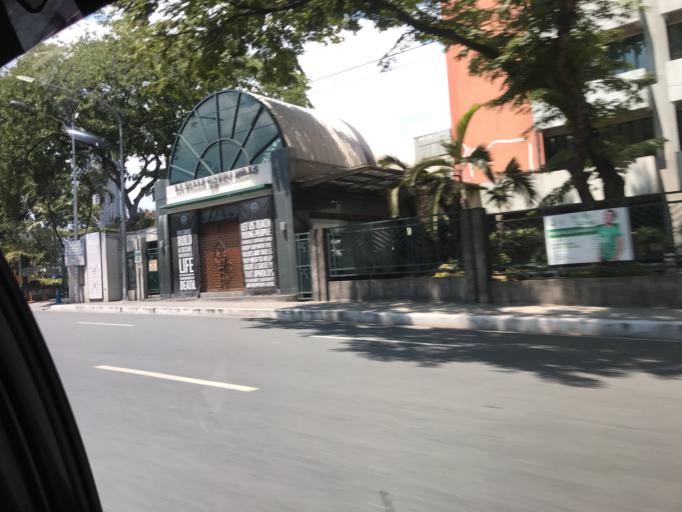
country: PH
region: Metro Manila
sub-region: Pasig
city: Pasig City
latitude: 14.5955
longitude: 121.0554
